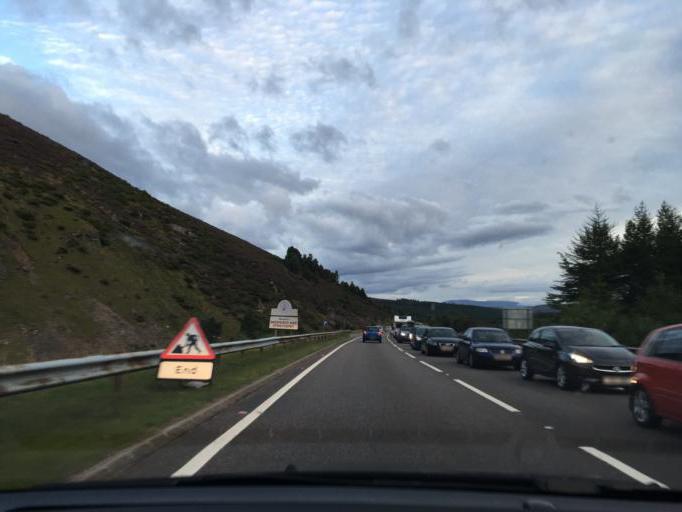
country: GB
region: Scotland
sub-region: Highland
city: Aviemore
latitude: 57.3017
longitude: -3.9266
